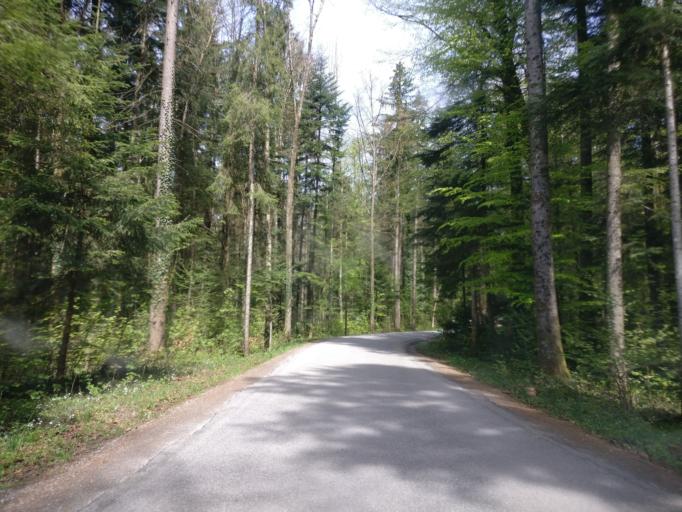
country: AT
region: Salzburg
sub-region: Politischer Bezirk Hallein
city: Kuchl
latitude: 47.6571
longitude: 13.1524
